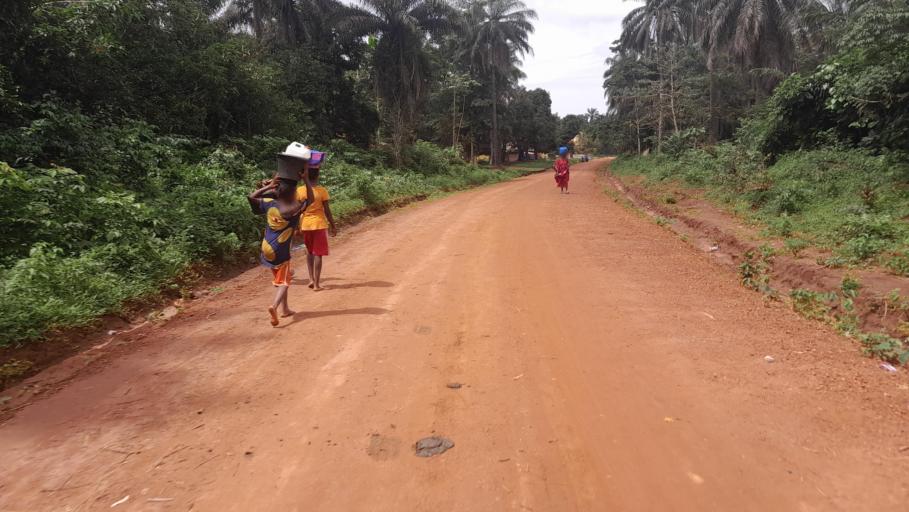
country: GN
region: Boke
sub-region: Boffa
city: Boffa
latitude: 10.0036
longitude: -13.8858
